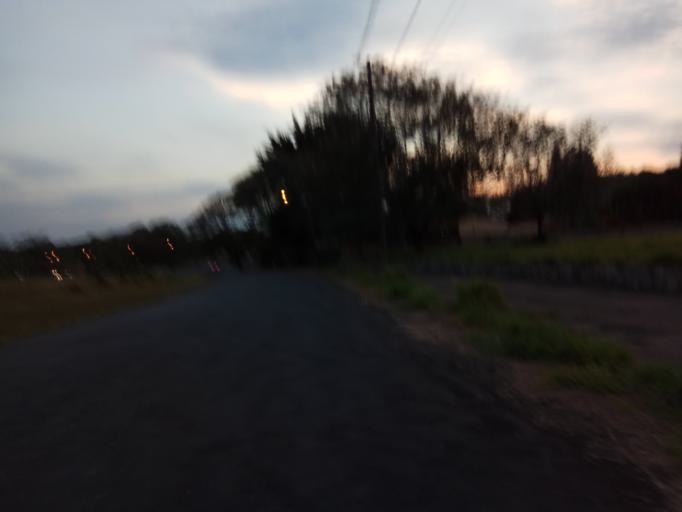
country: BR
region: Sao Paulo
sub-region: Piracicaba
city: Piracicaba
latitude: -22.7545
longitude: -47.5864
